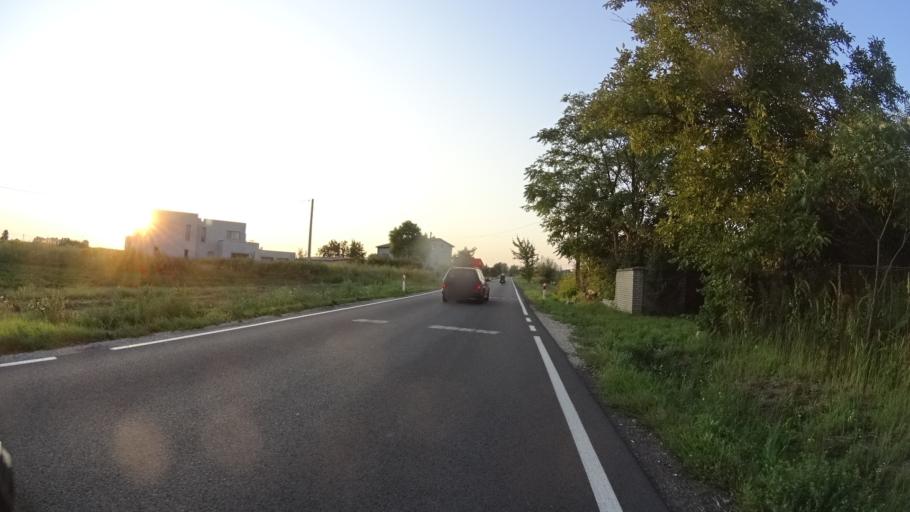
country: PL
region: Masovian Voivodeship
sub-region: Powiat warszawski zachodni
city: Ozarow Mazowiecki
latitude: 52.2426
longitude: 20.7492
